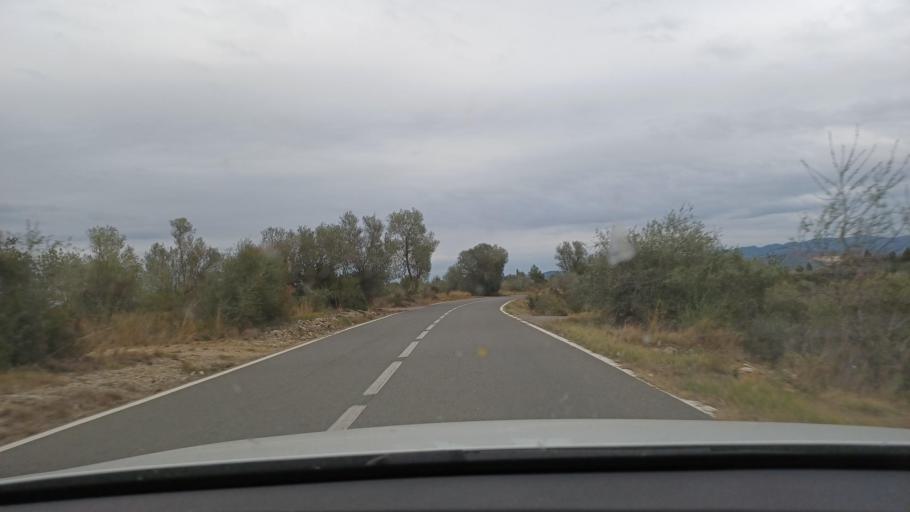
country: ES
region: Catalonia
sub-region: Provincia de Tarragona
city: Ulldecona
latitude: 40.6152
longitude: 0.3531
